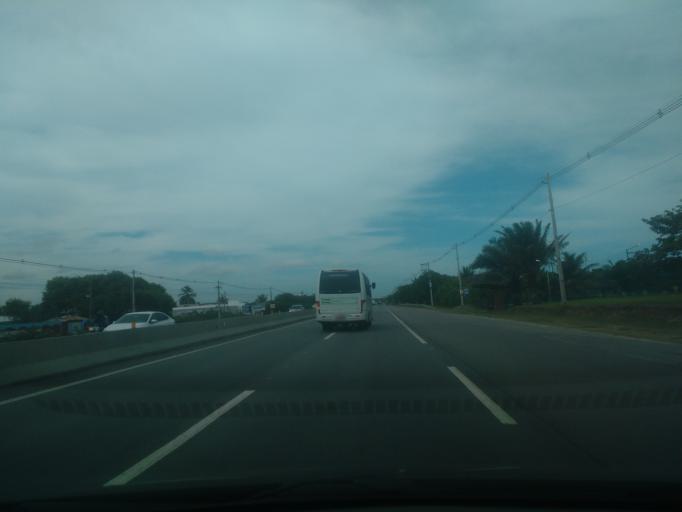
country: BR
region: Alagoas
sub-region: Maceio
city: Maceio
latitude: -9.7018
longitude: -35.8032
